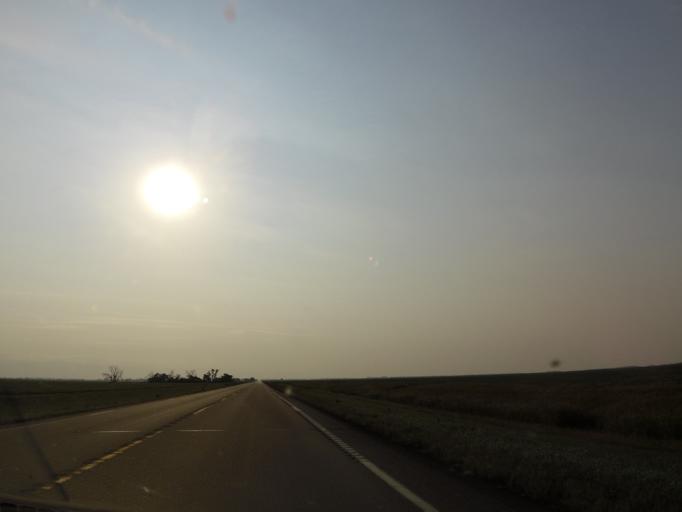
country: US
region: North Dakota
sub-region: Traill County
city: Hillsboro
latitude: 47.3528
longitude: -97.1707
